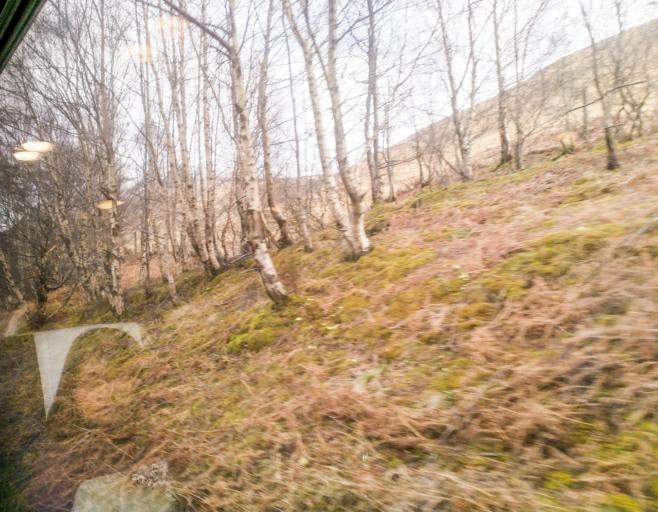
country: GB
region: Scotland
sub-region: Highland
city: Spean Bridge
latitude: 56.8087
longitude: -4.7181
